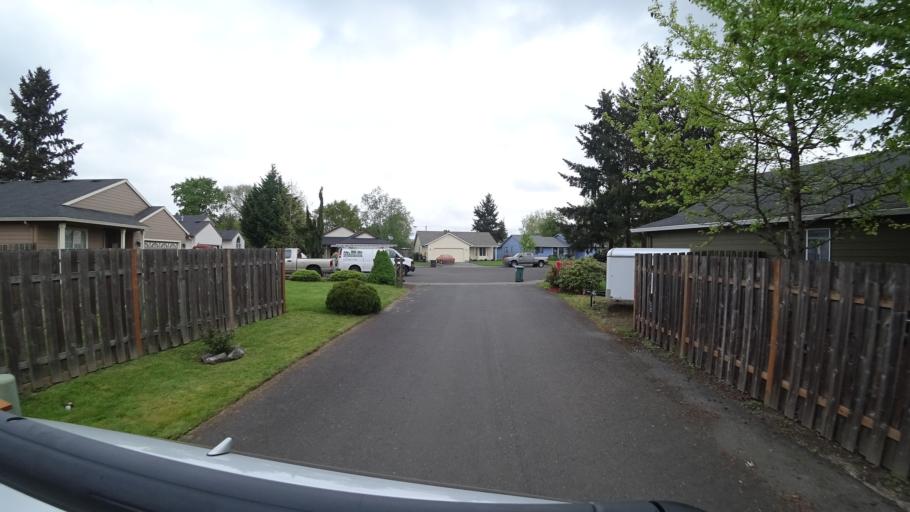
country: US
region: Oregon
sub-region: Washington County
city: Hillsboro
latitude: 45.5354
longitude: -122.9691
